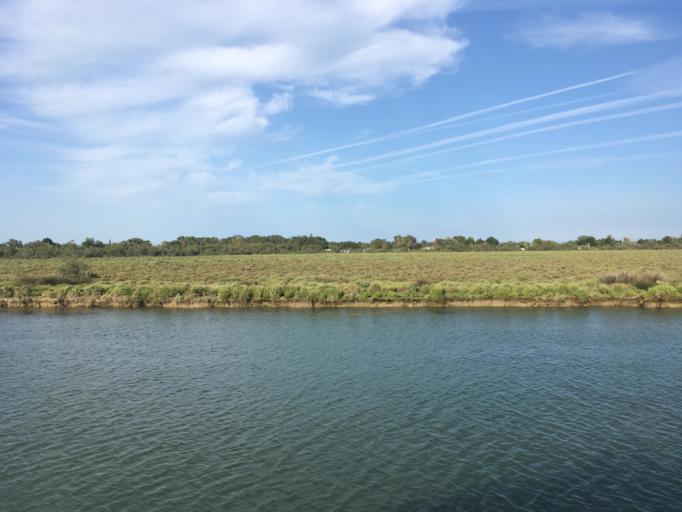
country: FR
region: Provence-Alpes-Cote d'Azur
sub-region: Departement des Bouches-du-Rhone
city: Saintes-Maries-de-la-Mer
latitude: 43.4732
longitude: 4.3876
